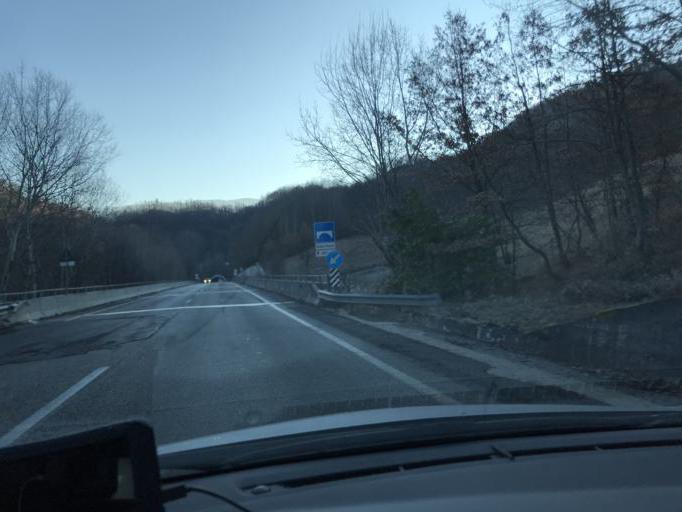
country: IT
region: Latium
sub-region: Provincia di Rieti
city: Fiamignano
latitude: 42.2542
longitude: 13.1455
